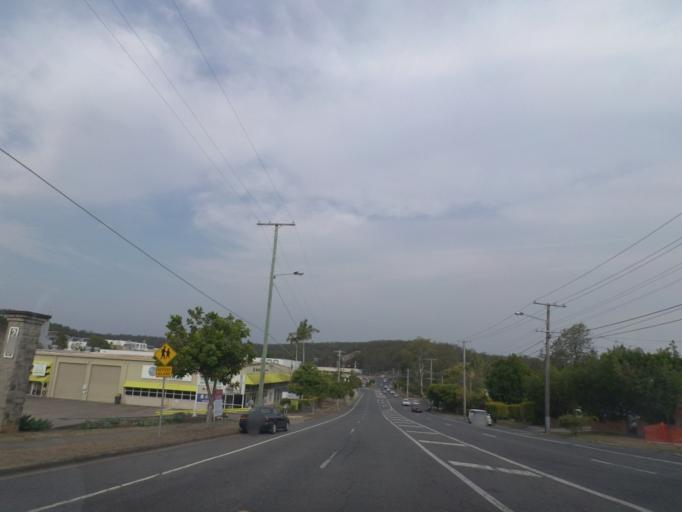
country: AU
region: Queensland
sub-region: Brisbane
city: Tarragindi
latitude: -27.5457
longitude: 153.0357
